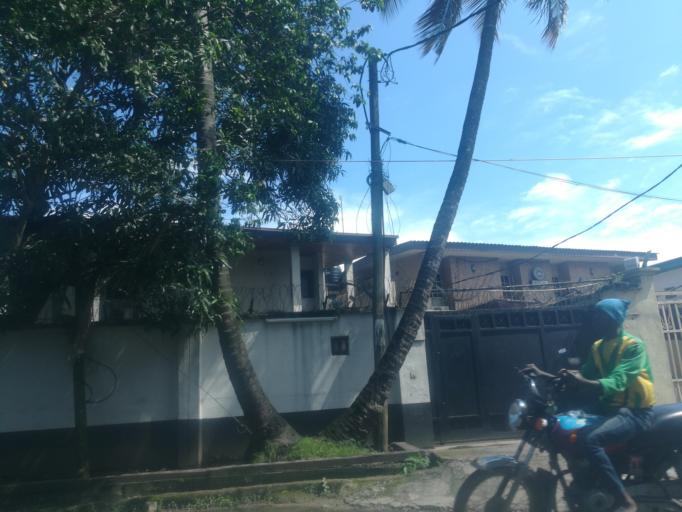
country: NG
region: Lagos
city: Somolu
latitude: 6.5503
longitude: 3.3750
